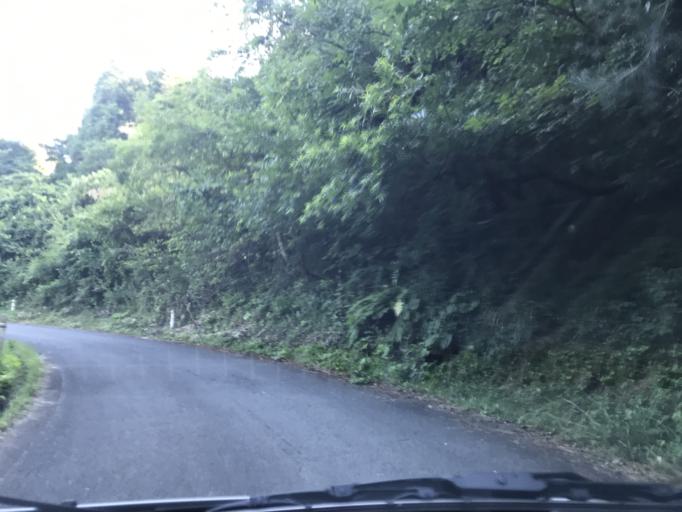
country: JP
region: Iwate
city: Mizusawa
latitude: 39.0685
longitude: 141.0438
